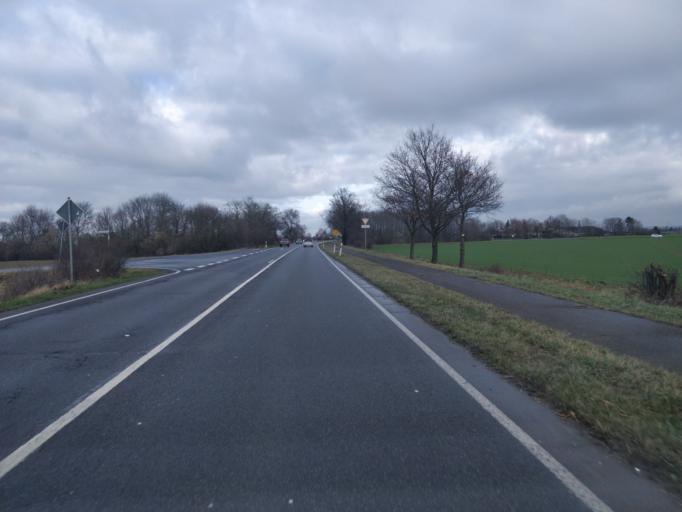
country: DE
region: North Rhine-Westphalia
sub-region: Regierungsbezirk Koln
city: Euskirchen
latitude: 50.6395
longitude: 6.8418
